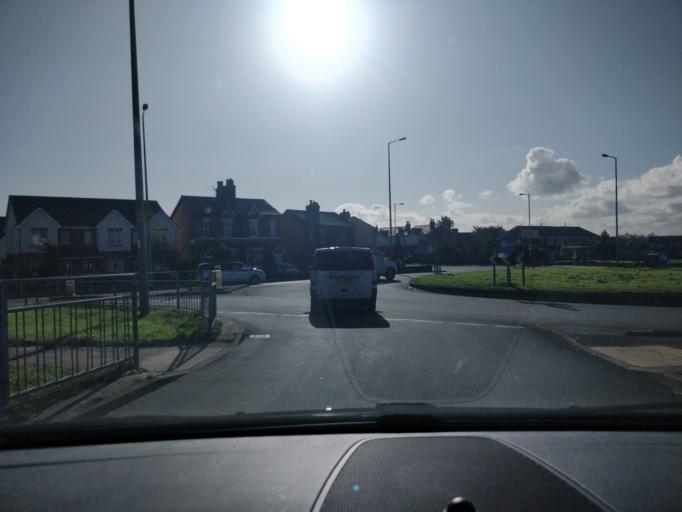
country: GB
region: England
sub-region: Lancashire
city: Banks
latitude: 53.6759
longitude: -2.9472
